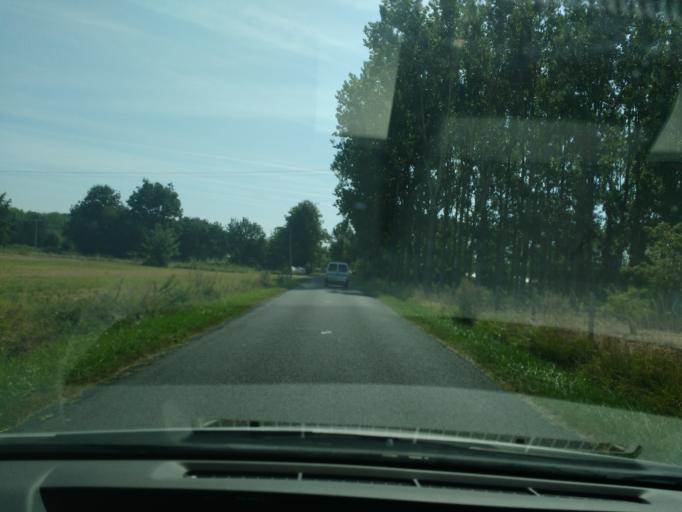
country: FR
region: Pays de la Loire
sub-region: Departement de Maine-et-Loire
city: Beaufort-en-Vallee
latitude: 47.4901
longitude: -0.2010
